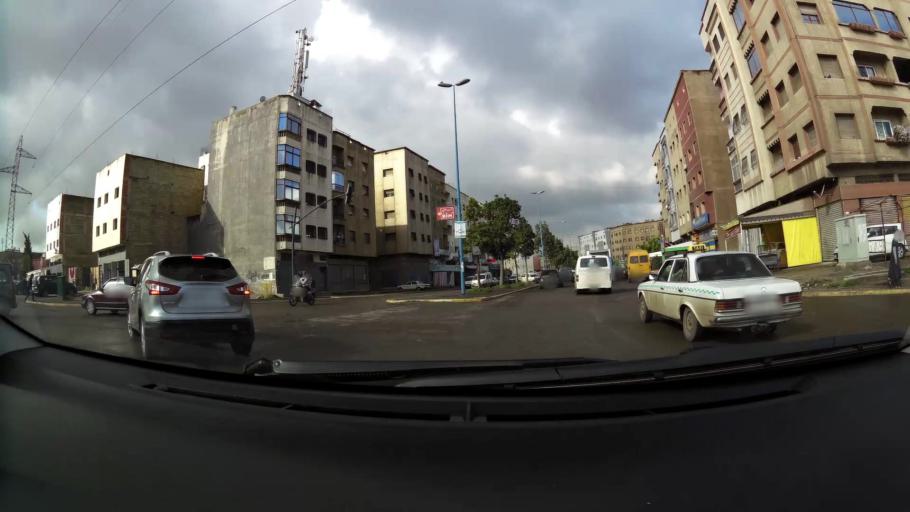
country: MA
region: Grand Casablanca
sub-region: Mediouna
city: Tit Mellil
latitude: 33.5879
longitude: -7.5241
